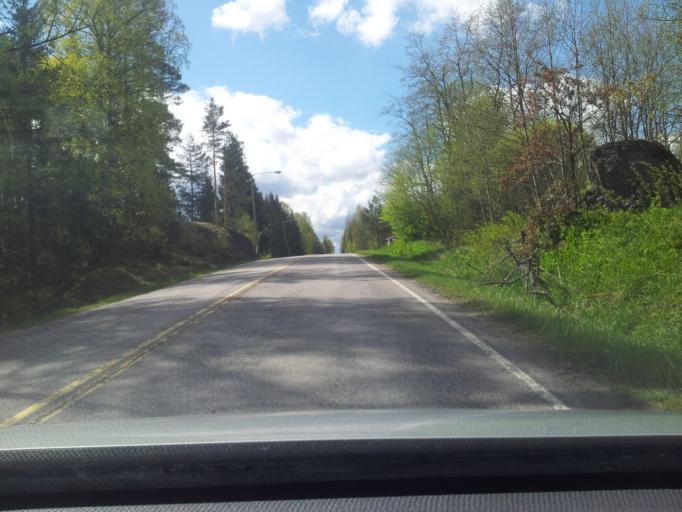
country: FI
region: Uusimaa
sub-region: Loviisa
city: Perna
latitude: 60.5005
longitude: 25.9217
